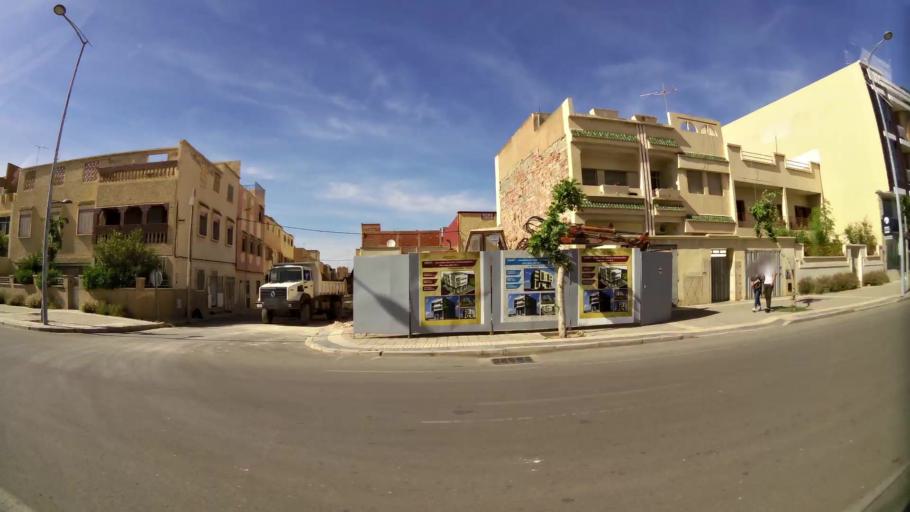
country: MA
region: Oriental
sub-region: Oujda-Angad
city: Oujda
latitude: 34.6651
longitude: -1.9112
